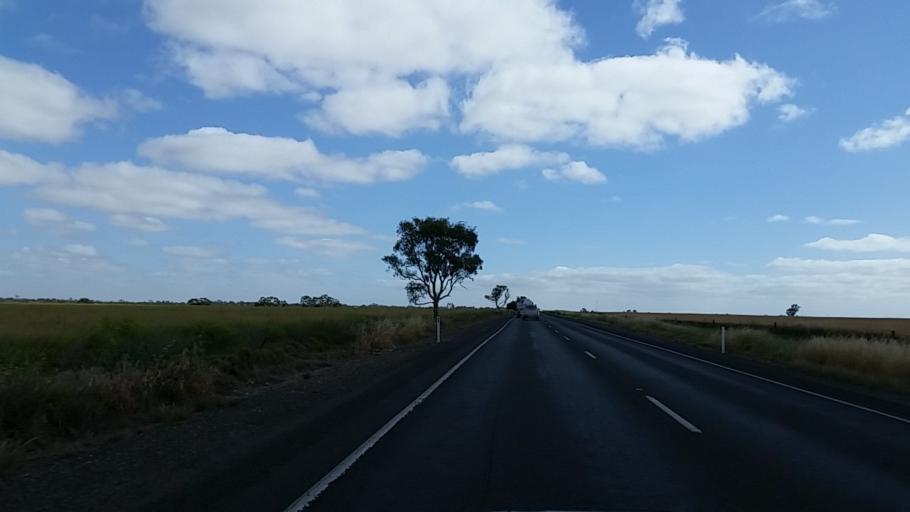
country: AU
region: South Australia
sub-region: Light
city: Willaston
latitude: -34.5638
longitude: 138.7467
